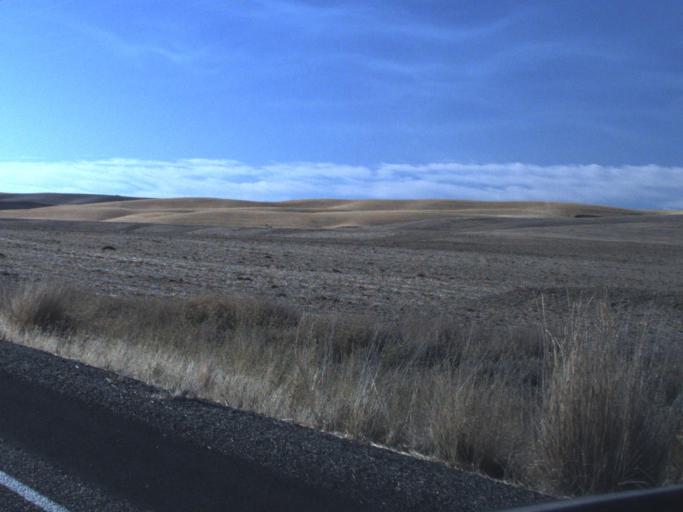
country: US
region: Washington
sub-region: Walla Walla County
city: Waitsburg
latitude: 46.3002
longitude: -118.3656
